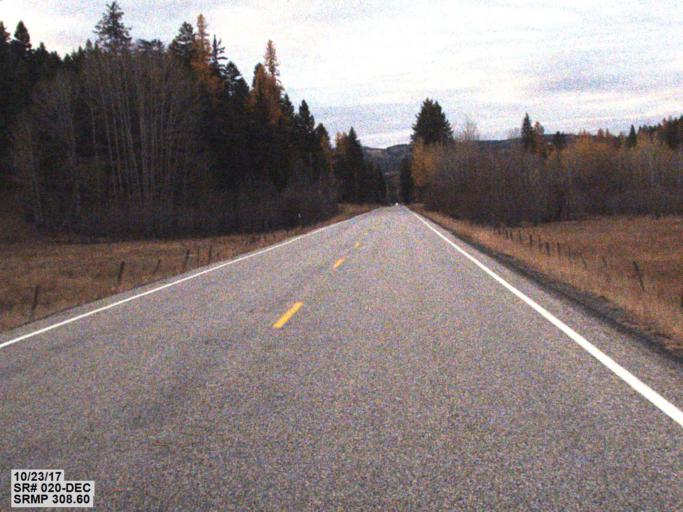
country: US
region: Washington
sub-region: Ferry County
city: Republic
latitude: 48.6070
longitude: -118.6588
